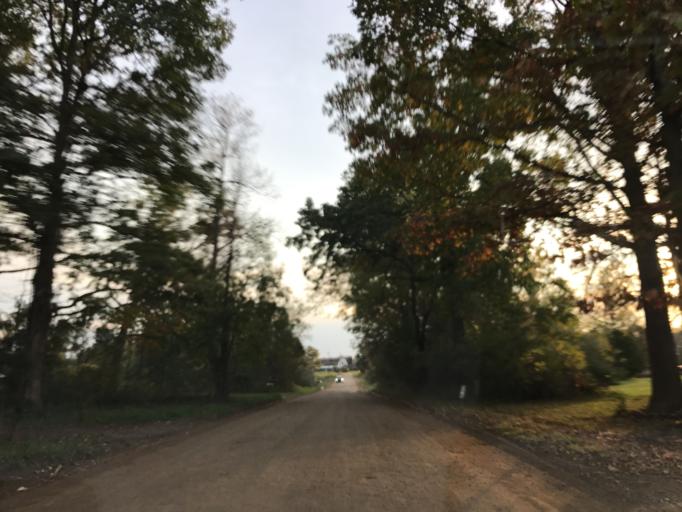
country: US
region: Michigan
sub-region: Oakland County
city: South Lyon
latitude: 42.4899
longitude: -83.6156
